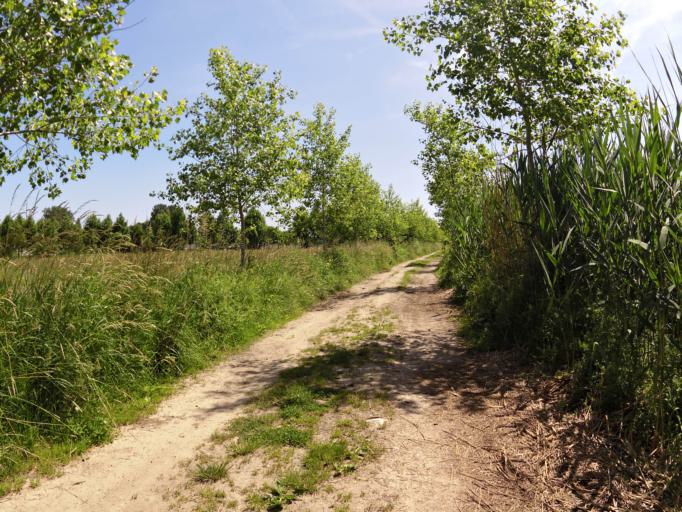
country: NL
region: North Brabant
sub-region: Gemeente Schijndel
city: Schijndel
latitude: 51.5825
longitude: 5.3956
